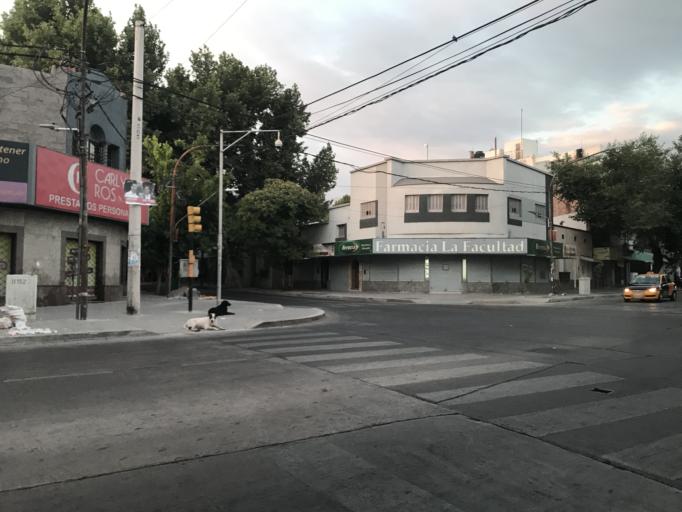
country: AR
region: Mendoza
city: Mendoza
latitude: -32.8927
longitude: -68.8344
